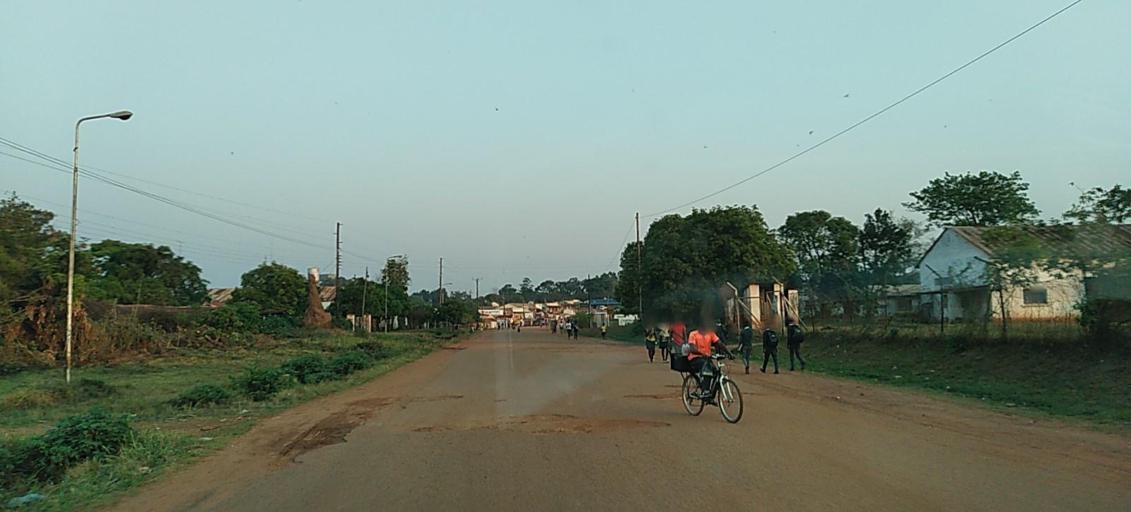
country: ZM
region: North-Western
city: Mwinilunga
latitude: -11.7296
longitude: 24.4291
